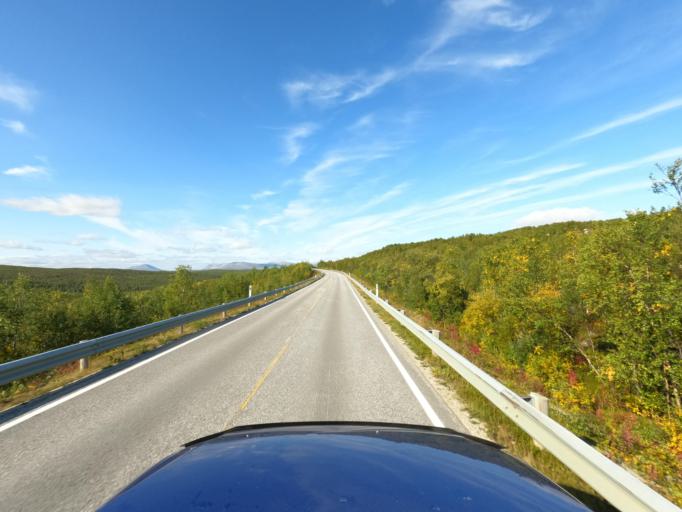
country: NO
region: Finnmark Fylke
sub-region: Porsanger
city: Lakselv
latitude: 69.7660
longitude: 25.1772
